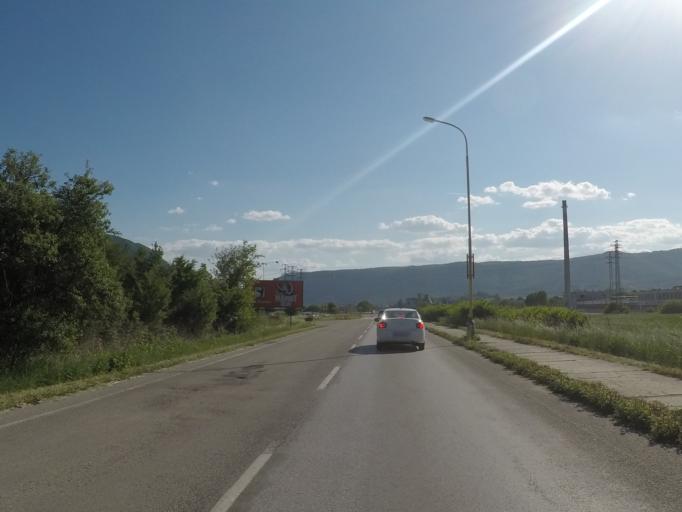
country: SK
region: Kosicky
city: Roznava
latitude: 48.6422
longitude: 20.5193
